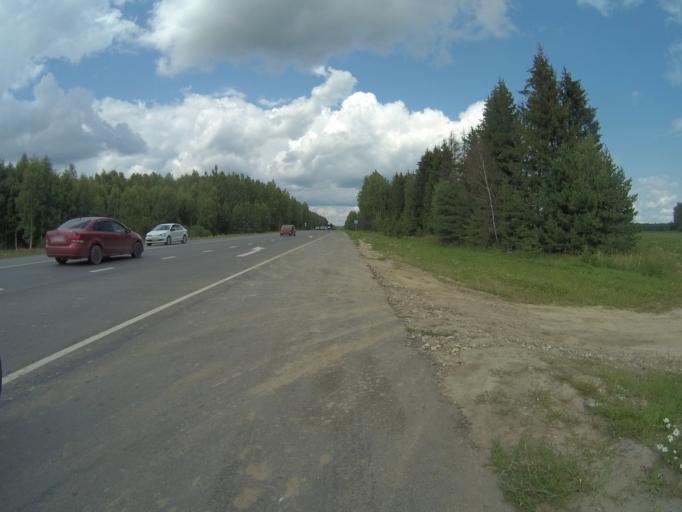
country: RU
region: Vladimir
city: Kideksha
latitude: 56.5933
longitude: 40.5557
